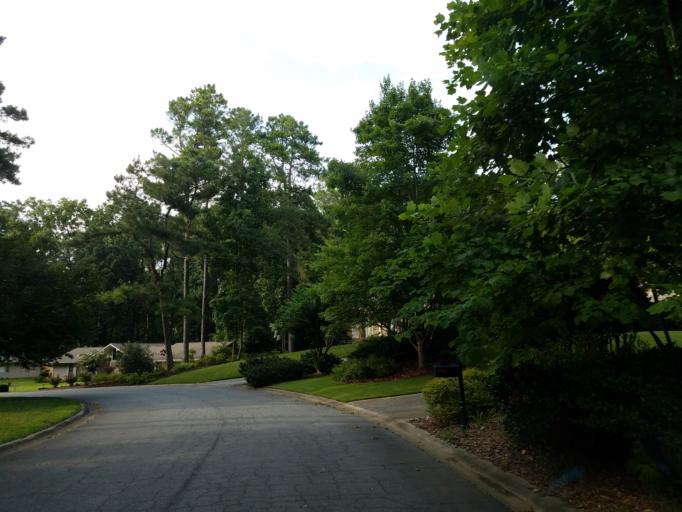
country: US
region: Georgia
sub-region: Fulton County
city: Sandy Springs
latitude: 33.9584
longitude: -84.4489
